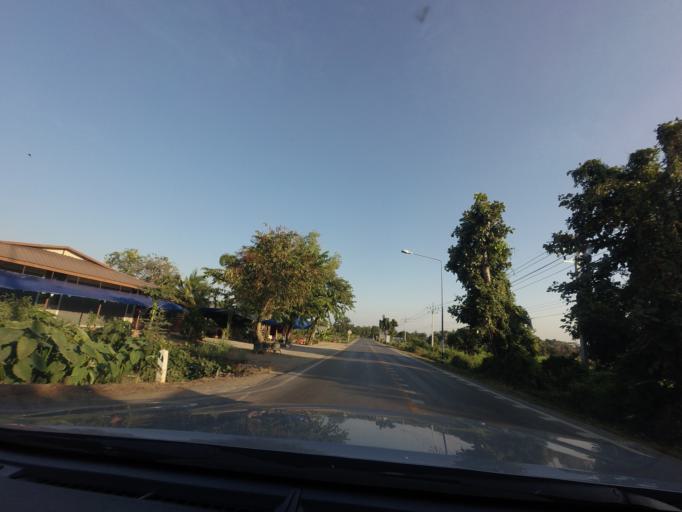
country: TH
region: Sukhothai
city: Sawankhalok
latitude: 17.3594
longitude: 99.8153
